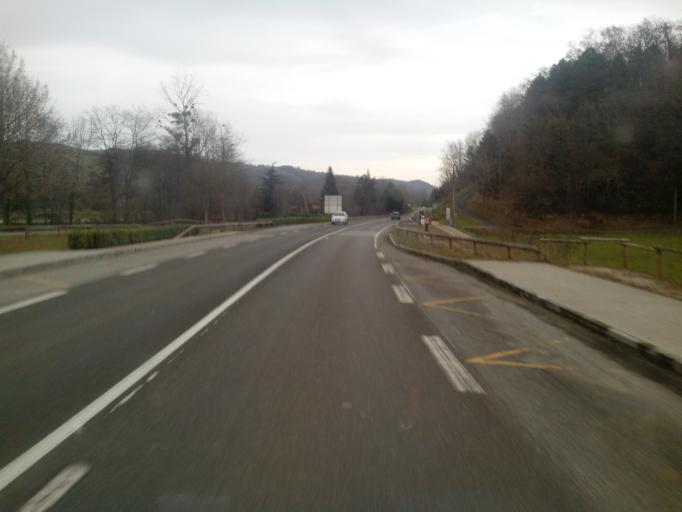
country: FR
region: Midi-Pyrenees
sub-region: Departement de l'Ariege
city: Montjoie-en-Couserans
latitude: 43.0170
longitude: 1.3731
